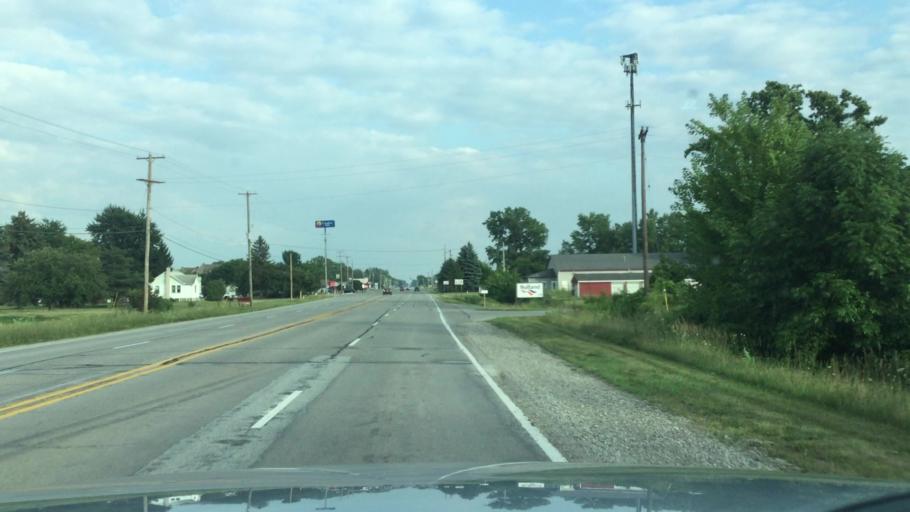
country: US
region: Michigan
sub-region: Saginaw County
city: Birch Run
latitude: 43.2546
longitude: -83.7728
